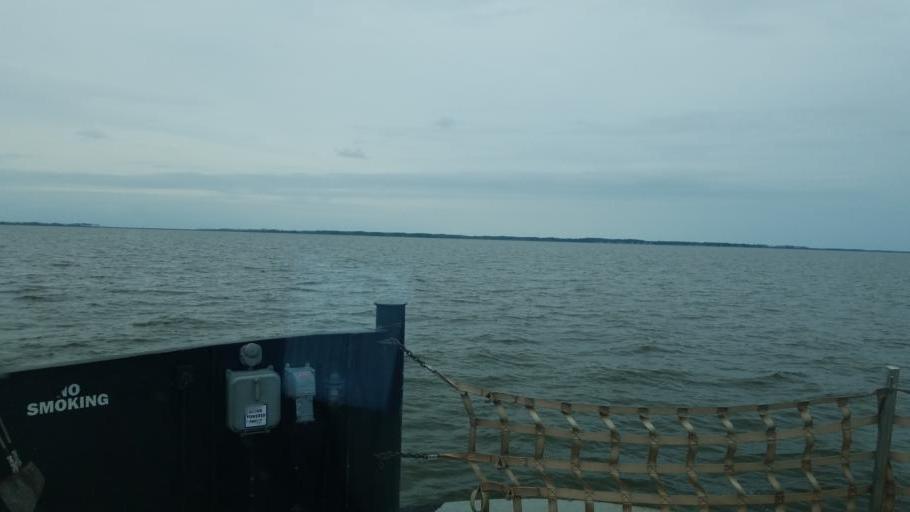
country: US
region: North Carolina
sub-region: Currituck County
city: Currituck
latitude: 36.4614
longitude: -75.9722
